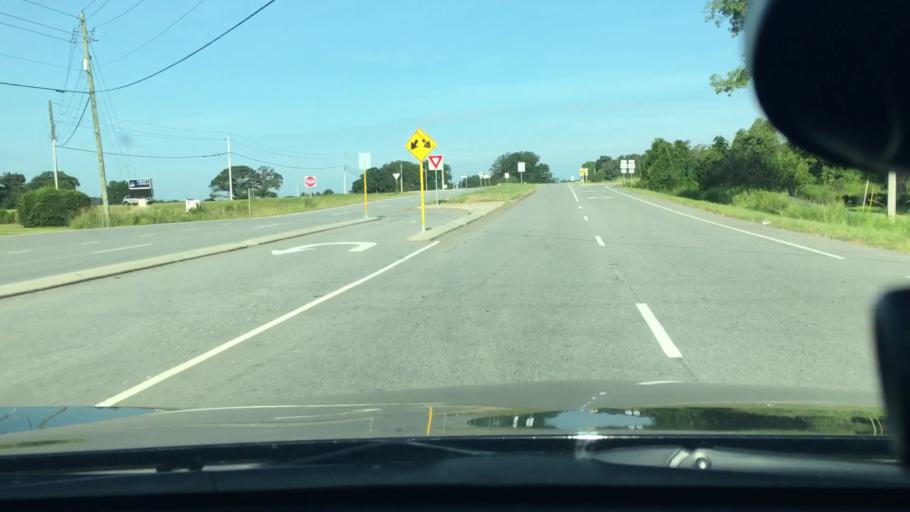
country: US
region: North Carolina
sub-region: Pitt County
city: Greenville
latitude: 35.6285
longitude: -77.4305
